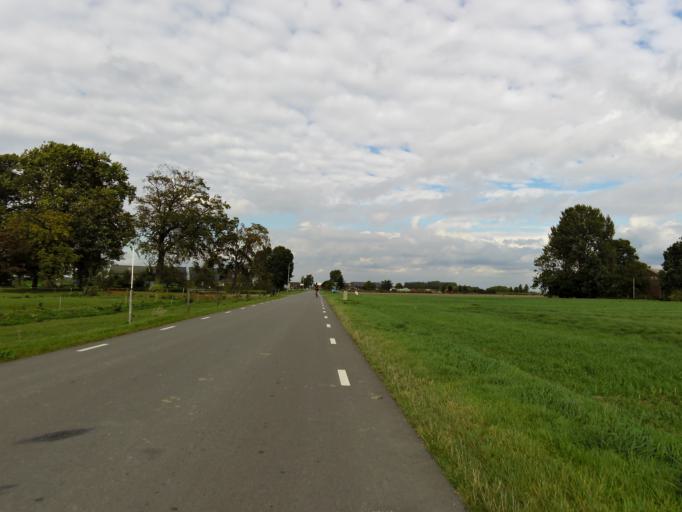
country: NL
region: South Holland
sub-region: Gemeente Rijnwoude
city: Benthuizen
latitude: 52.0557
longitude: 4.5755
